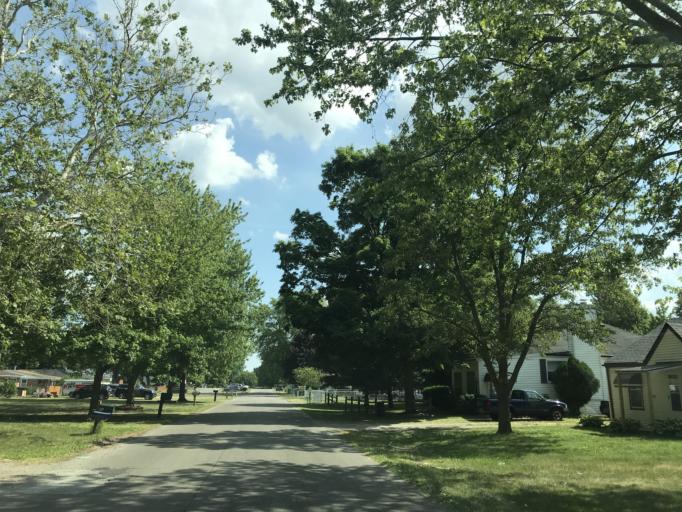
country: US
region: Michigan
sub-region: Washtenaw County
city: Ypsilanti
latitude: 42.2529
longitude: -83.5820
